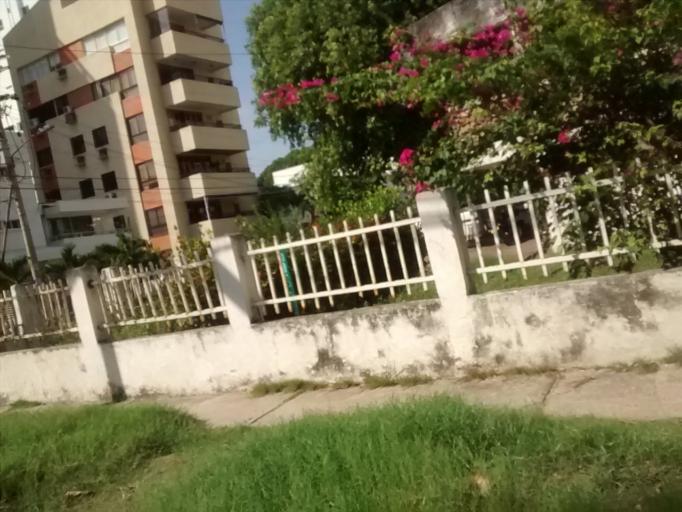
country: CO
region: Bolivar
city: Cartagena
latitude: 10.3932
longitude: -75.5495
